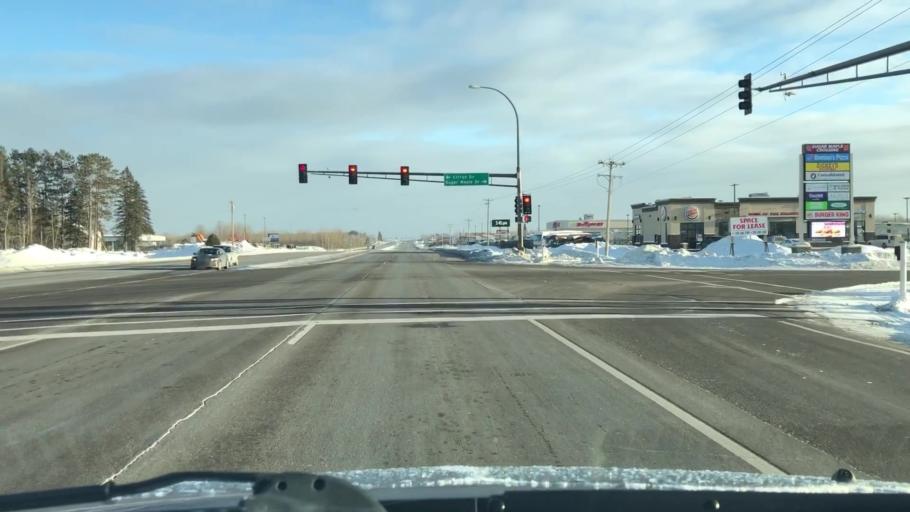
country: US
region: Minnesota
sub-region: Saint Louis County
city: Hermantown
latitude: 46.8337
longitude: -92.2057
